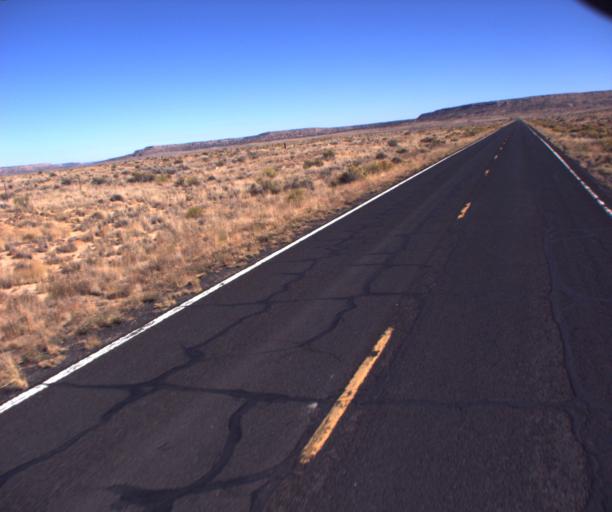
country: US
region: Arizona
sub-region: Navajo County
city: First Mesa
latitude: 35.8408
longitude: -110.3424
